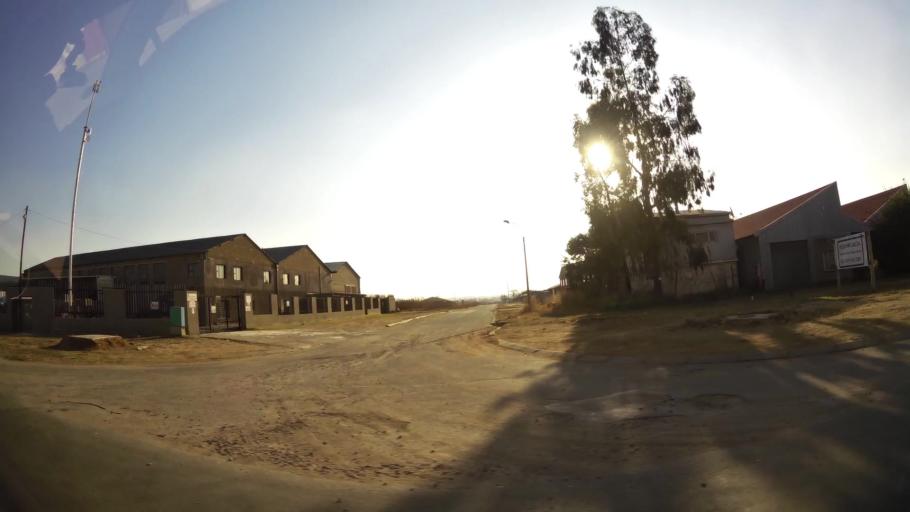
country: ZA
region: Gauteng
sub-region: West Rand District Municipality
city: Randfontein
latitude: -26.2028
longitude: 27.6954
